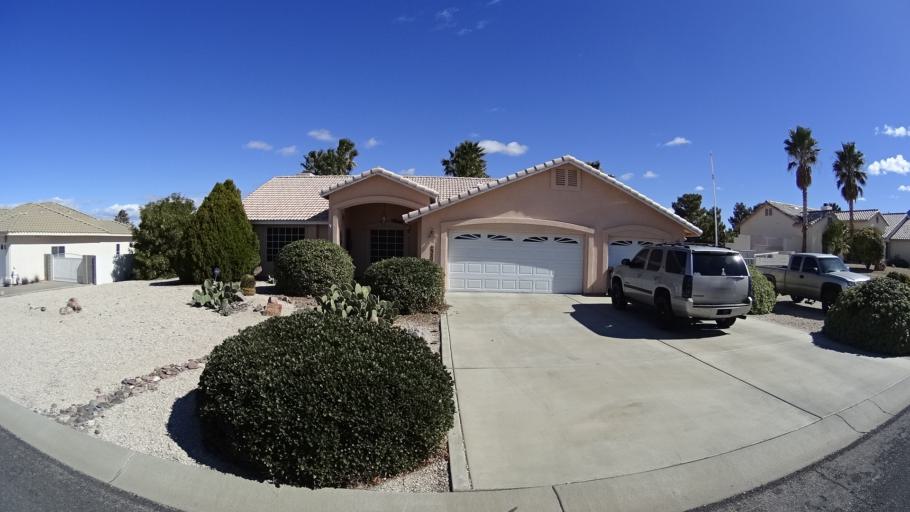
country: US
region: Arizona
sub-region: Mohave County
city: Kingman
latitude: 35.2030
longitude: -113.9636
